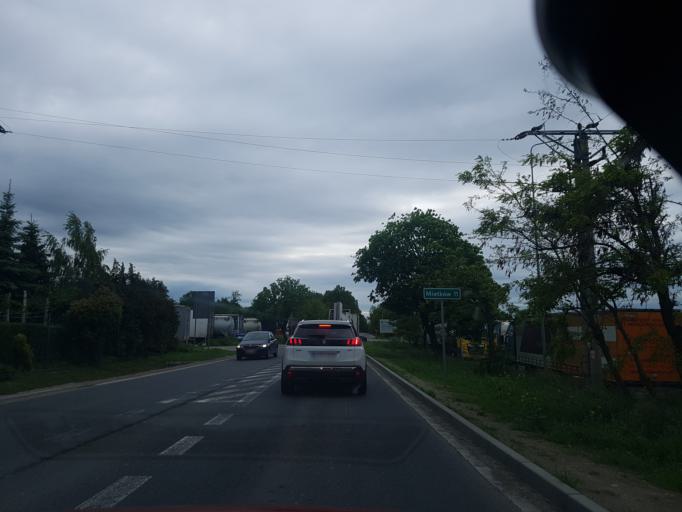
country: PL
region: Lower Silesian Voivodeship
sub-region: Powiat wroclawski
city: Katy Wroclawskie
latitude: 51.0180
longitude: 16.7538
